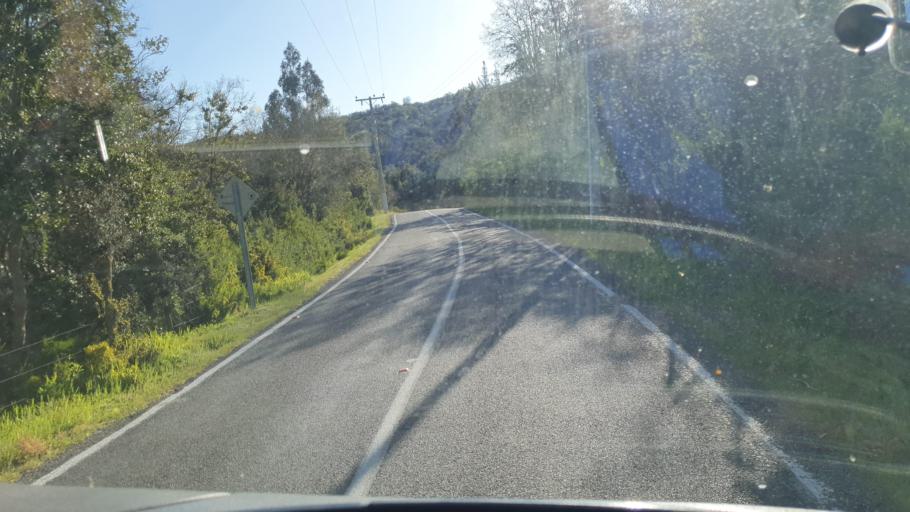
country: CL
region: Valparaiso
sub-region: Provincia de Marga Marga
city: Limache
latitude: -33.1958
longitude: -71.2164
